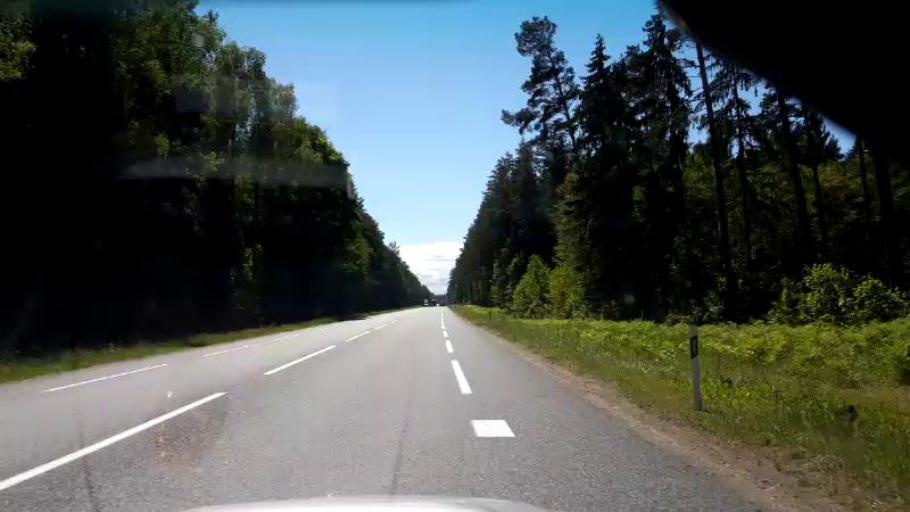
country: LV
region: Saulkrastu
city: Saulkrasti
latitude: 57.3642
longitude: 24.4371
